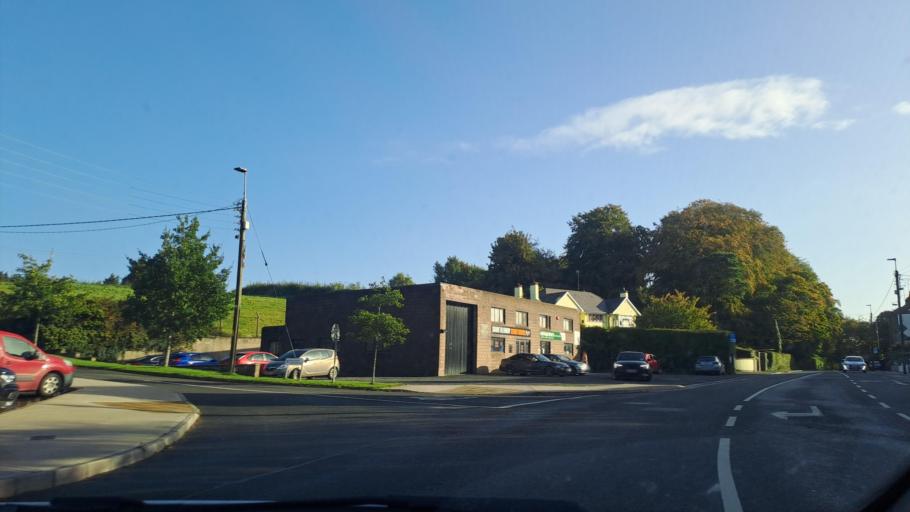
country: IE
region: Ulster
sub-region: County Monaghan
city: Monaghan
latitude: 54.2547
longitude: -6.9648
